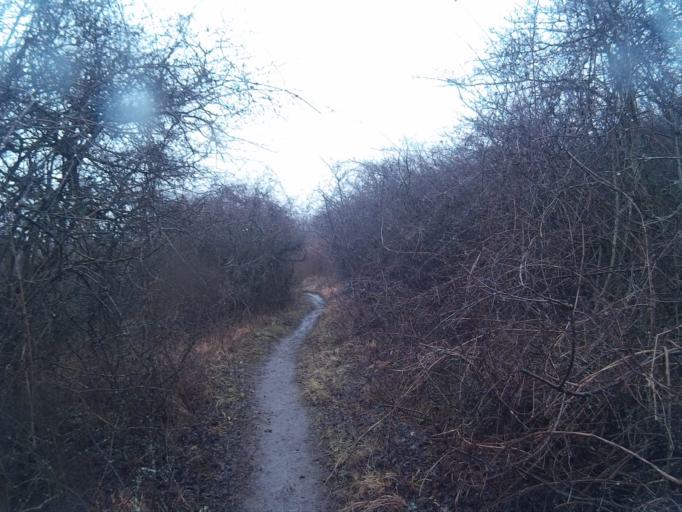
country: HU
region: Komarom-Esztergom
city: Tokod
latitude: 47.7149
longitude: 18.6364
